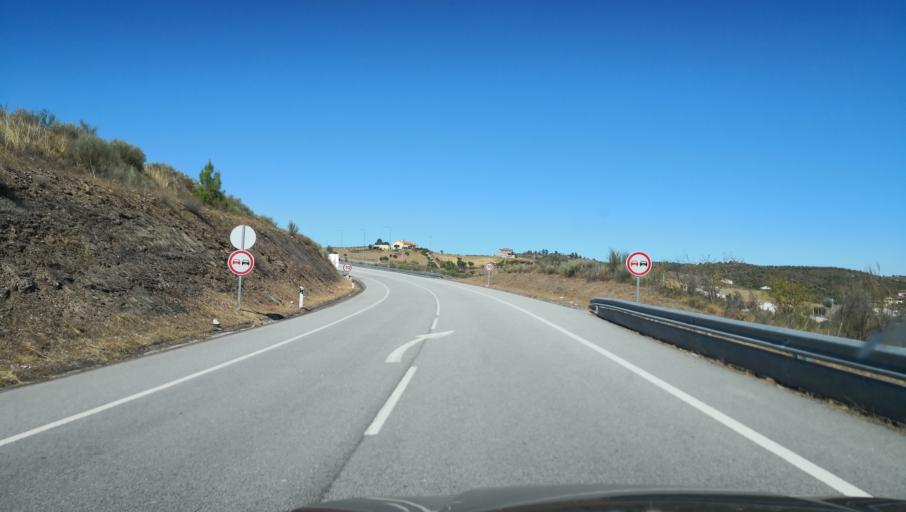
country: PT
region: Braganca
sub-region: Mirandela
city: Mirandela
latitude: 41.5133
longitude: -7.2270
